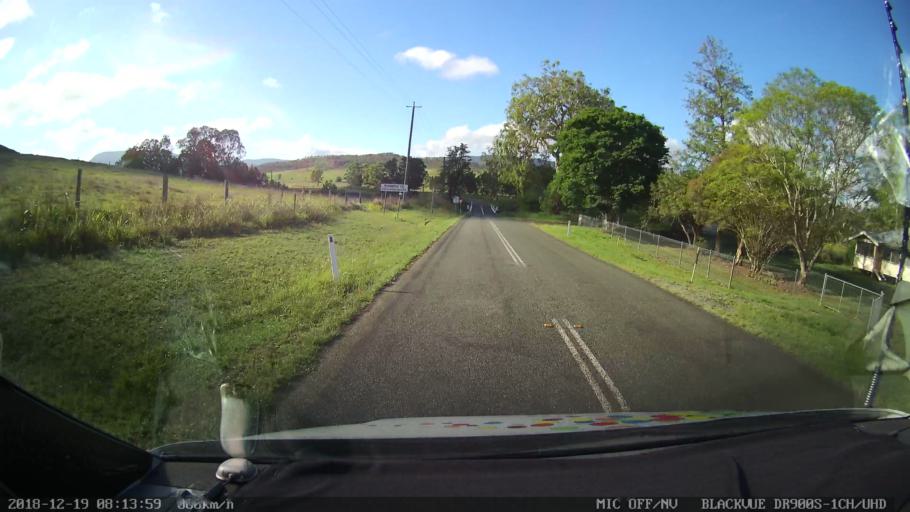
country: AU
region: Queensland
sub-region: Logan
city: Cedar Vale
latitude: -28.2438
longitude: 152.8900
